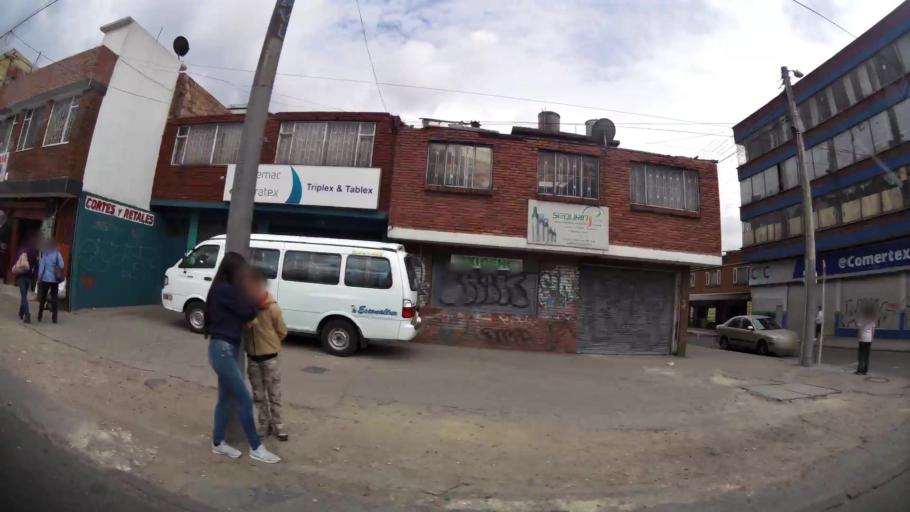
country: CO
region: Bogota D.C.
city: Bogota
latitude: 4.5997
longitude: -74.1350
